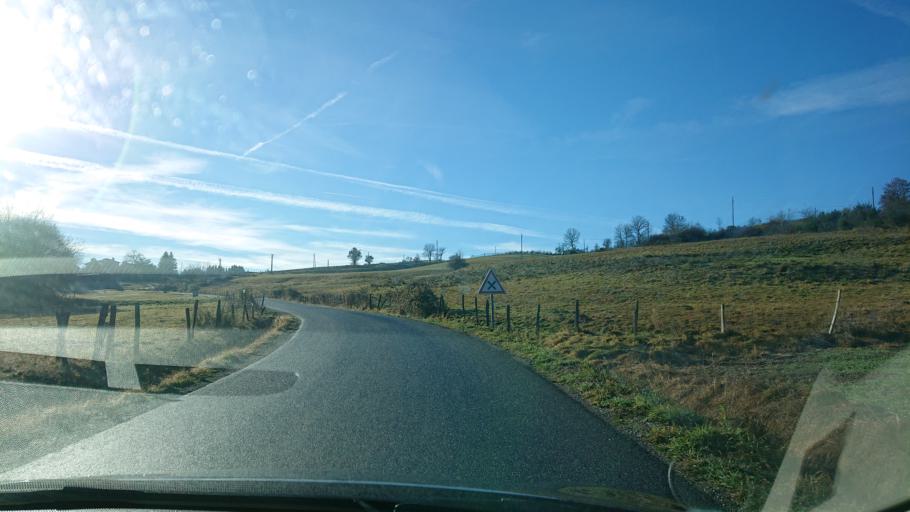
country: FR
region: Auvergne
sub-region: Departement de la Haute-Loire
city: Vorey
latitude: 45.2253
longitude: 3.9373
